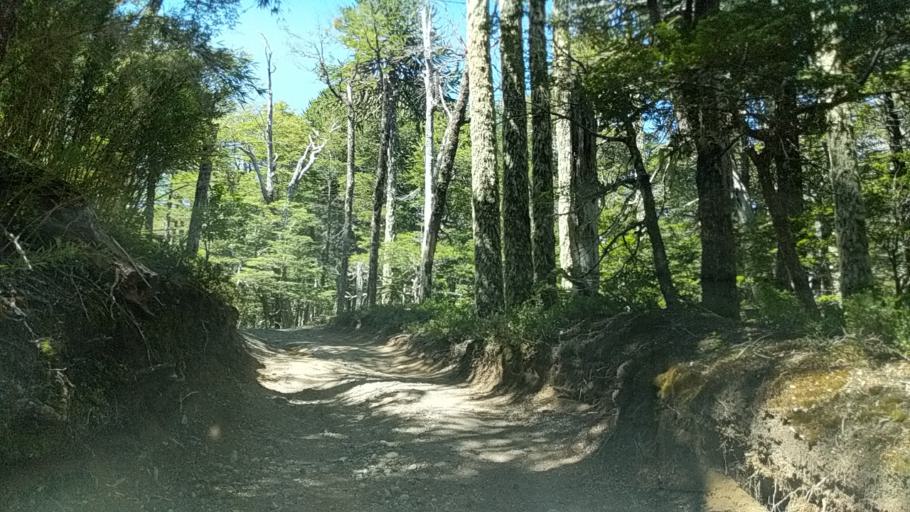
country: CL
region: Araucania
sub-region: Provincia de Cautin
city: Pucon
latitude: -39.4660
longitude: -71.8528
